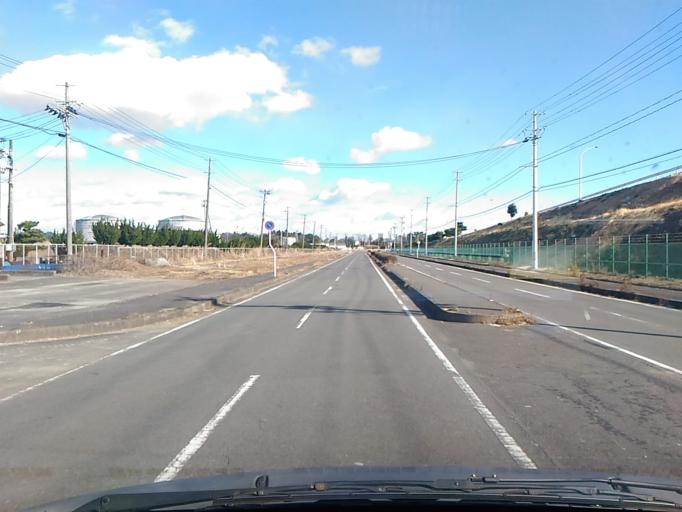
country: JP
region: Fukushima
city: Iwaki
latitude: 36.9289
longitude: 140.8553
